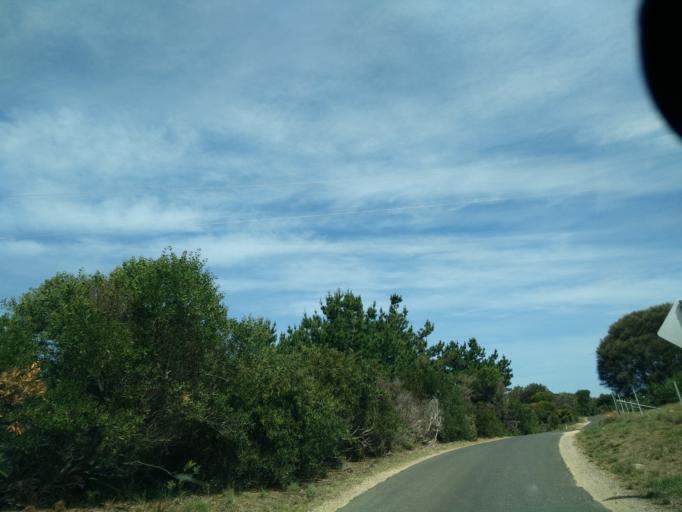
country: AU
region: Tasmania
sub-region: Break O'Day
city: St Helens
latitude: -41.1707
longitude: 148.2793
